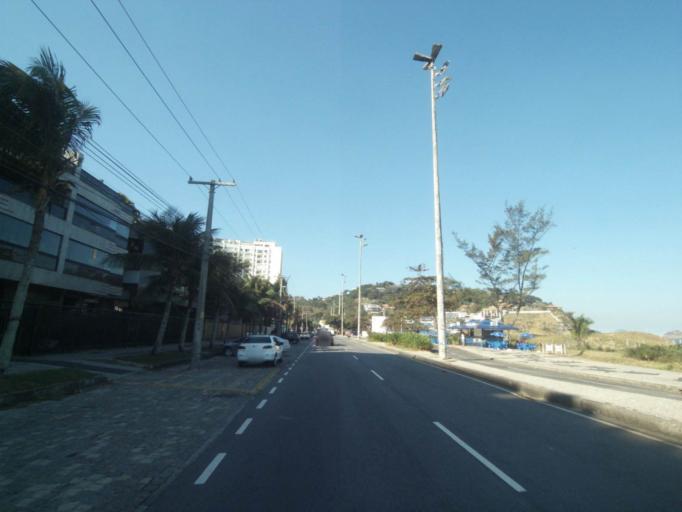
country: BR
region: Rio de Janeiro
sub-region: Rio De Janeiro
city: Rio de Janeiro
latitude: -23.0145
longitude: -43.3008
